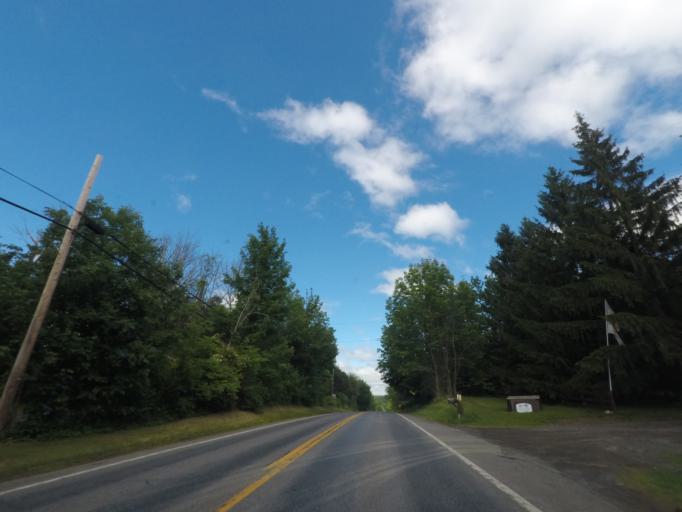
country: US
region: New York
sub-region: Columbia County
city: Philmont
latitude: 42.2089
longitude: -73.6544
